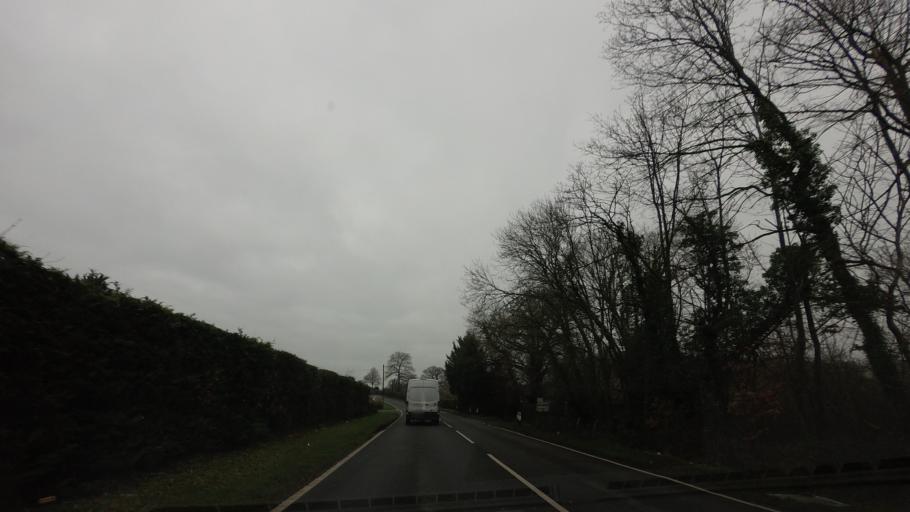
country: GB
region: England
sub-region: Kent
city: Staplehurst
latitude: 51.1465
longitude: 0.5515
